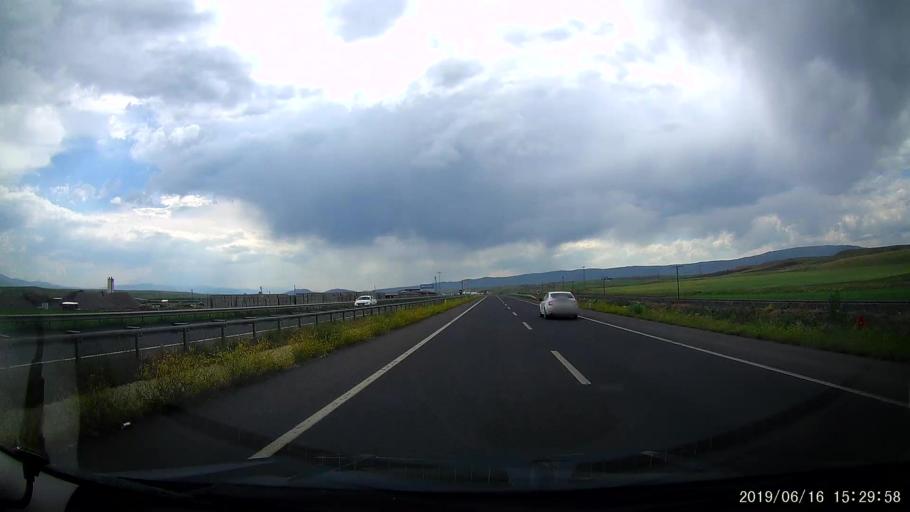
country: TR
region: Erzurum
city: Horasan
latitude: 40.0327
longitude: 42.1188
